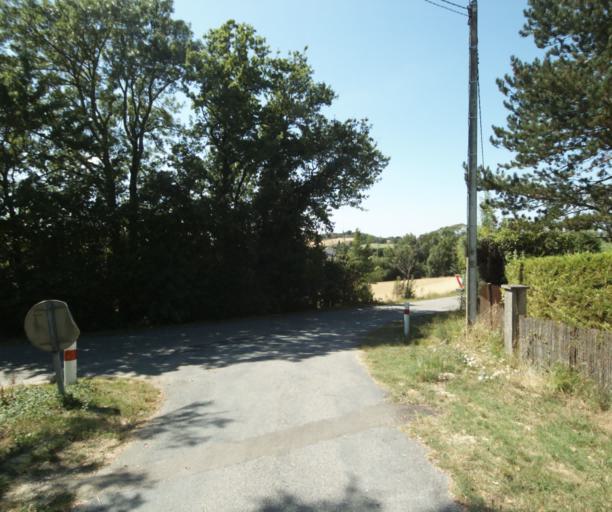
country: FR
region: Midi-Pyrenees
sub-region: Departement de la Haute-Garonne
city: Saint-Felix-Lauragais
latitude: 43.4934
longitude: 1.8973
